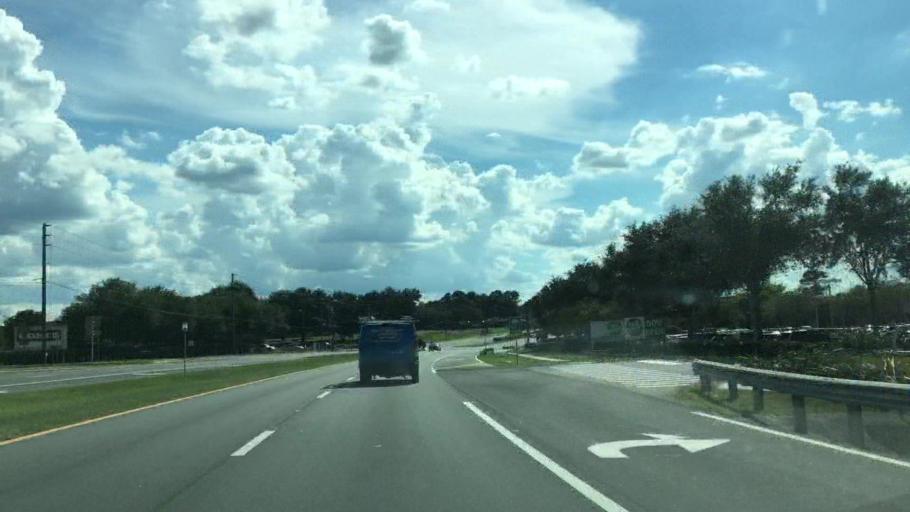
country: US
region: Florida
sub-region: Seminole County
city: Lake Mary
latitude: 28.7960
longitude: -81.3342
